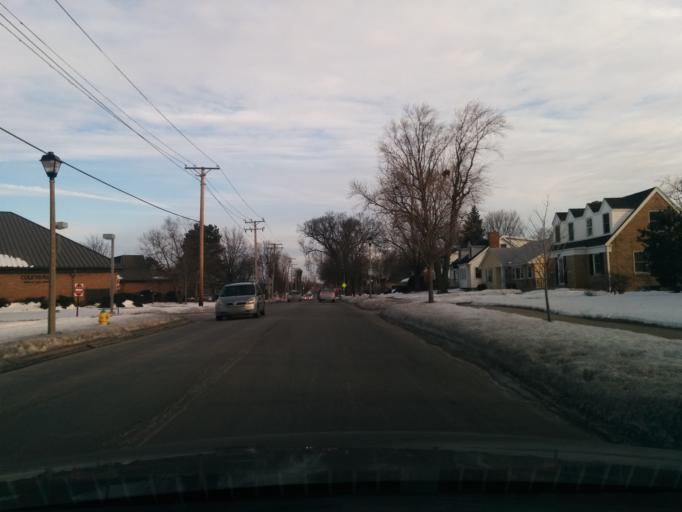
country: US
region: Illinois
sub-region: DuPage County
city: Elmhurst
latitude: 41.8945
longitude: -87.9593
